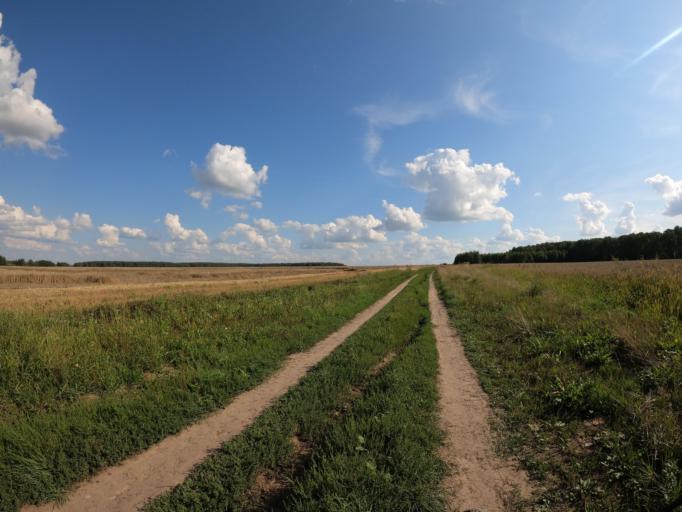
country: RU
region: Moskovskaya
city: Troitskoye
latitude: 55.2295
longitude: 38.4854
